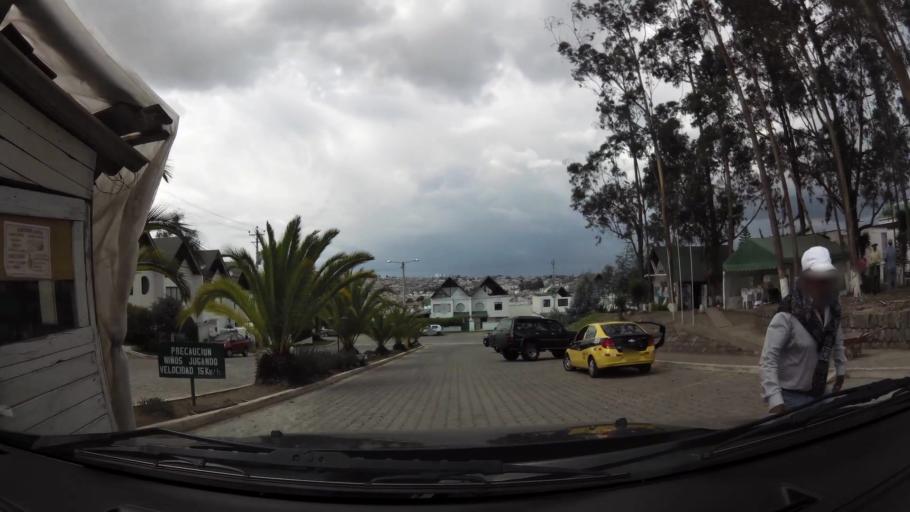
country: EC
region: Pichincha
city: Quito
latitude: -0.0980
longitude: -78.4606
